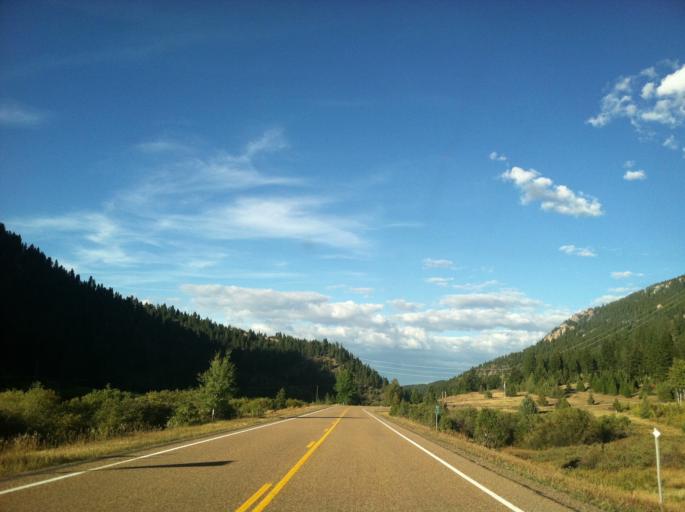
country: US
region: Montana
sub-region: Granite County
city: Philipsburg
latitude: 46.4362
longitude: -113.2657
